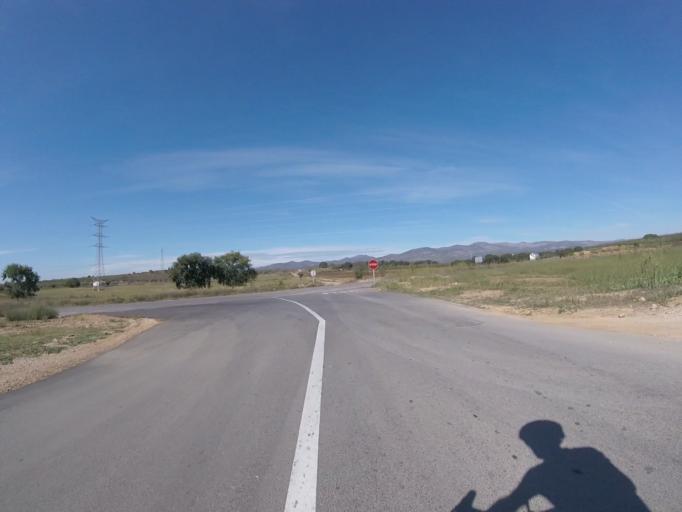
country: ES
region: Valencia
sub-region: Provincia de Castello
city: Benlloch
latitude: 40.2083
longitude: 0.0447
